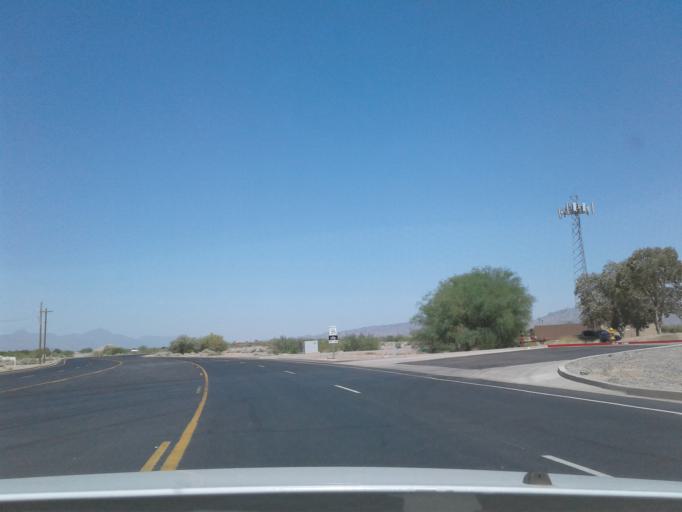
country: US
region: Arizona
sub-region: Maricopa County
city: Guadalupe
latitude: 33.2626
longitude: -111.9750
